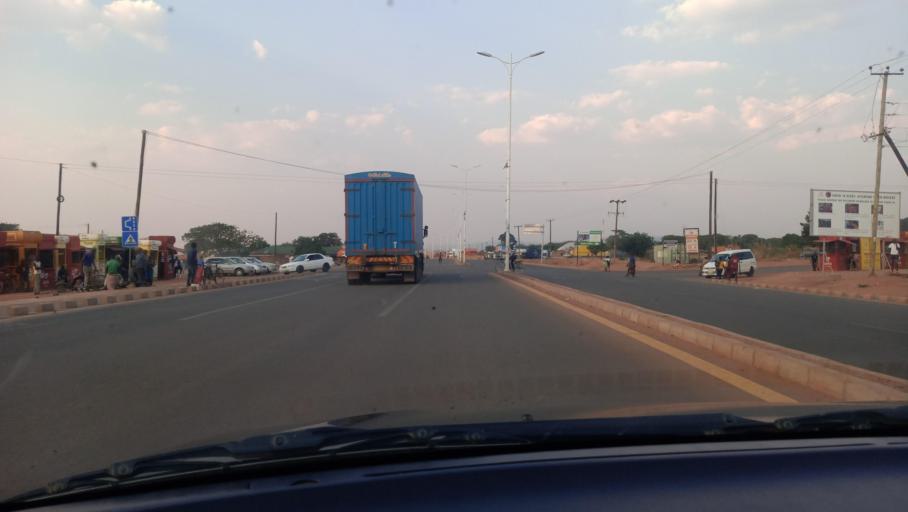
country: ZM
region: Northern
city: Mpika
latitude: -11.8367
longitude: 31.4464
